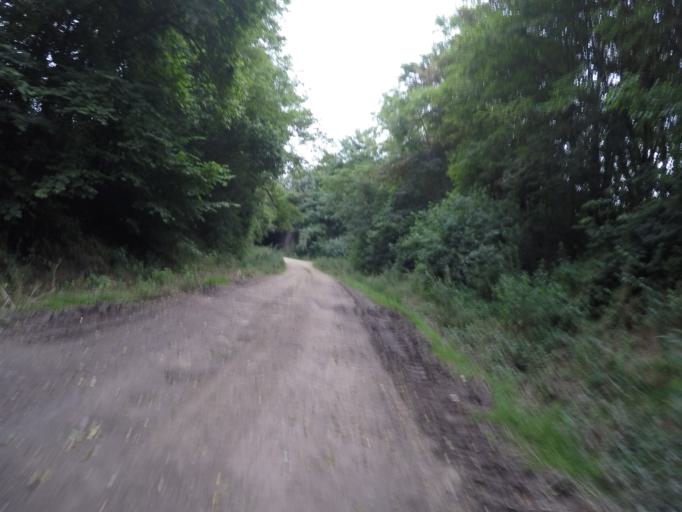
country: BE
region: Wallonia
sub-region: Province de Namur
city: Assesse
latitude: 50.3006
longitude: 5.0147
